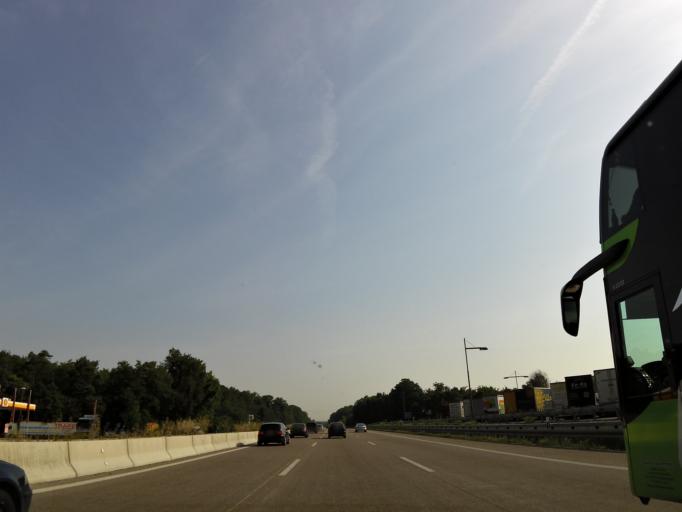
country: DE
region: Baden-Wuerttemberg
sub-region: Karlsruhe Region
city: Forst
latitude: 49.1623
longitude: 8.5693
